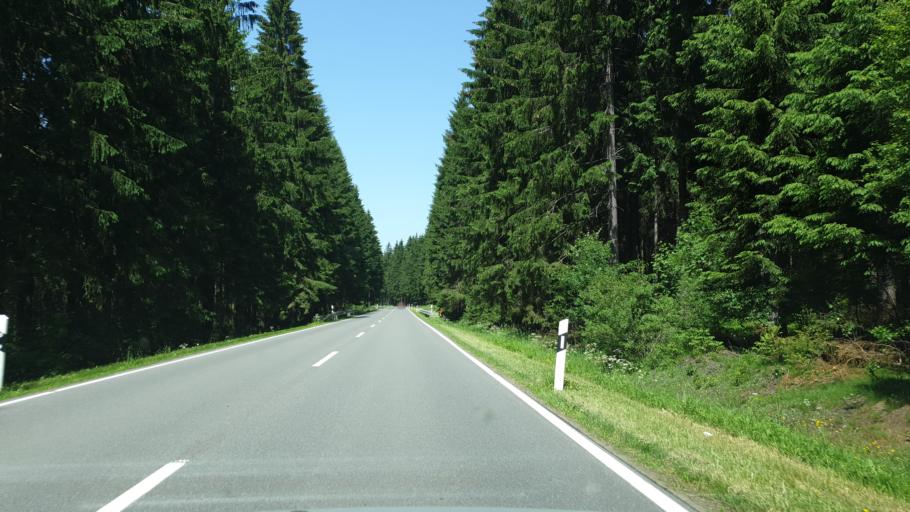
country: DE
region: Saxony
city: Hammerbrucke
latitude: 50.4045
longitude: 12.4217
